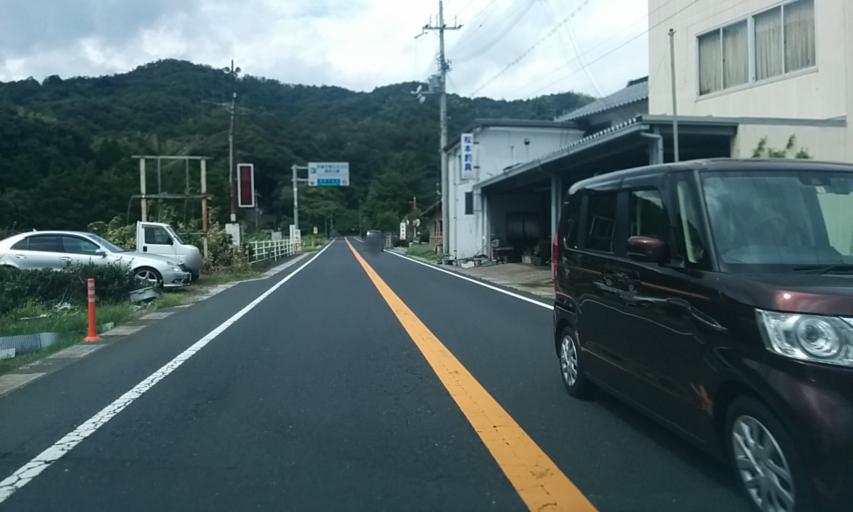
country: JP
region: Kyoto
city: Miyazu
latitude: 35.5229
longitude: 135.2737
